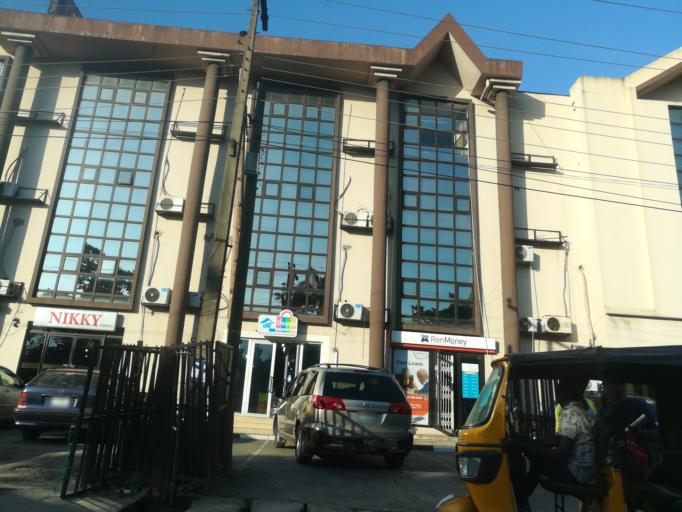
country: NG
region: Lagos
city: Ikeja
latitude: 6.5934
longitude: 3.3578
